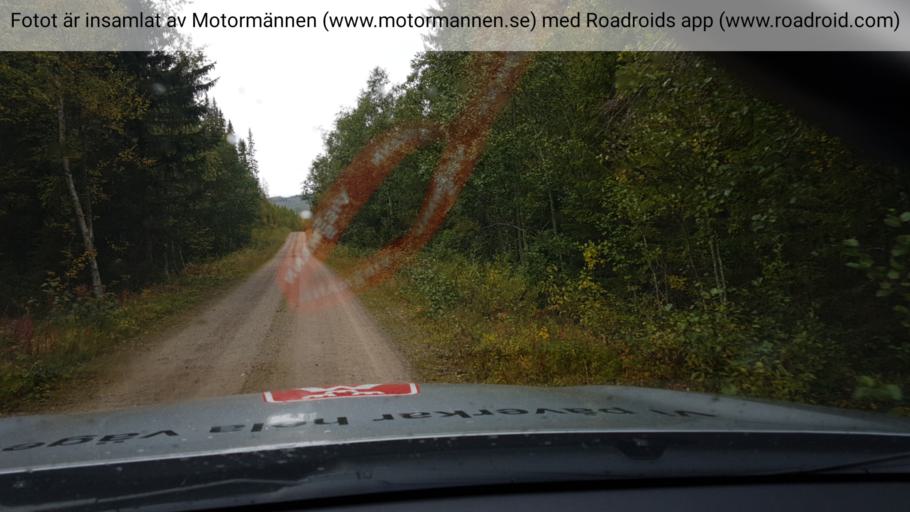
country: SE
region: Jaemtland
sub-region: Harjedalens Kommun
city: Sveg
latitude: 62.2501
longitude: 13.2858
